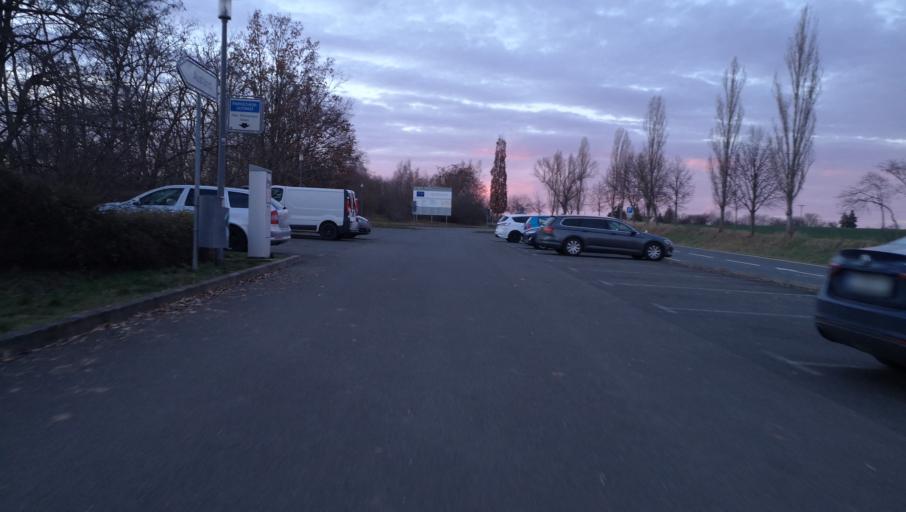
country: DE
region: Thuringia
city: Ronneburg
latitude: 50.8621
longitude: 12.1681
